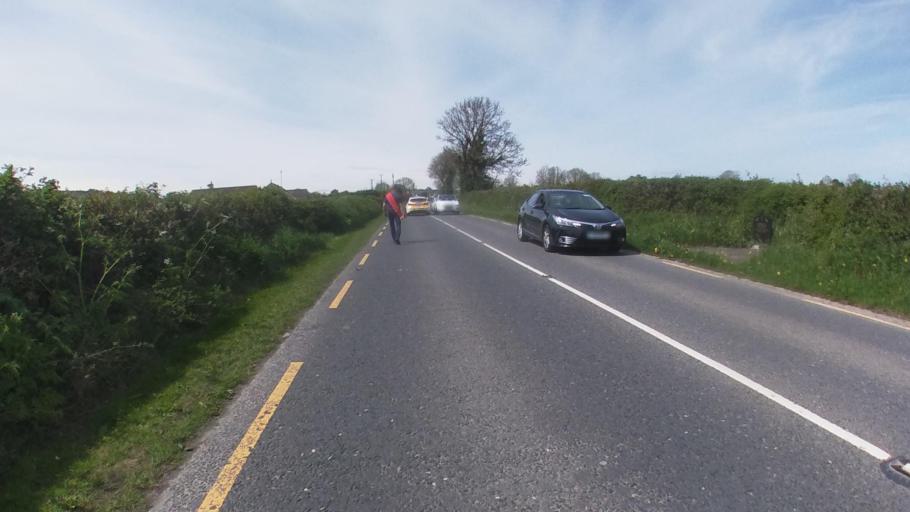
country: IE
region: Leinster
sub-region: County Carlow
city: Carlow
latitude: 52.8452
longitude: -6.9842
